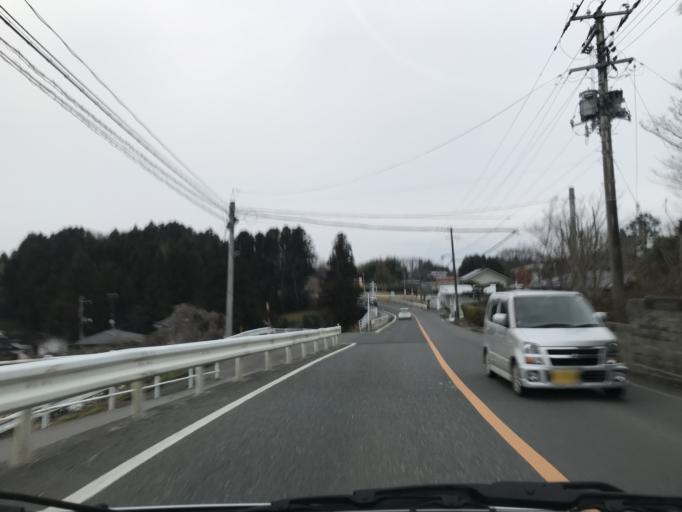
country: JP
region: Miyagi
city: Wakuya
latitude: 38.6925
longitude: 141.1458
